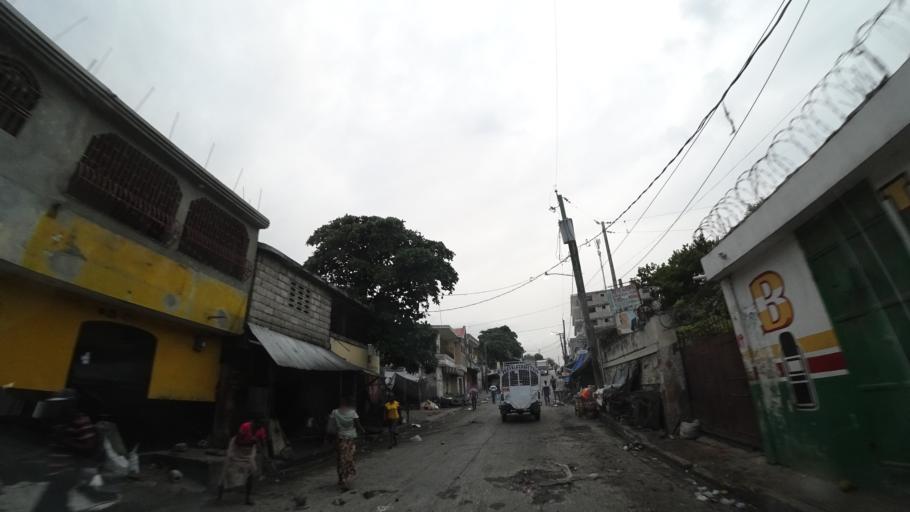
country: HT
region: Ouest
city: Delmas 73
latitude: 18.5429
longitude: -72.3171
